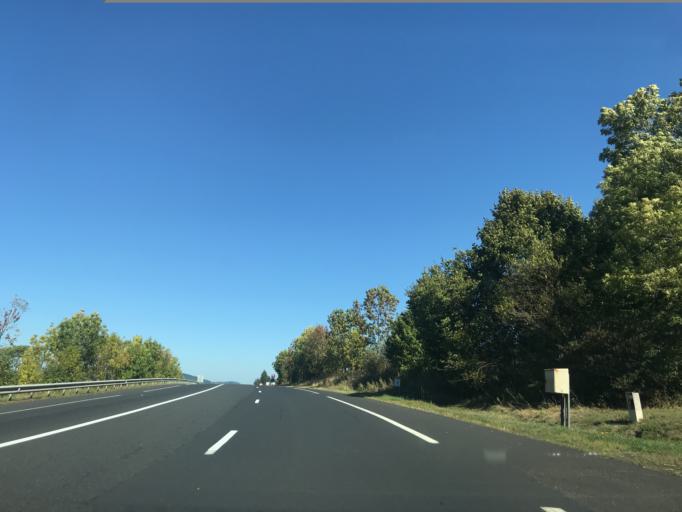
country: FR
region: Auvergne
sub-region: Departement du Puy-de-Dome
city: Gelles
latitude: 45.6785
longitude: 2.7977
